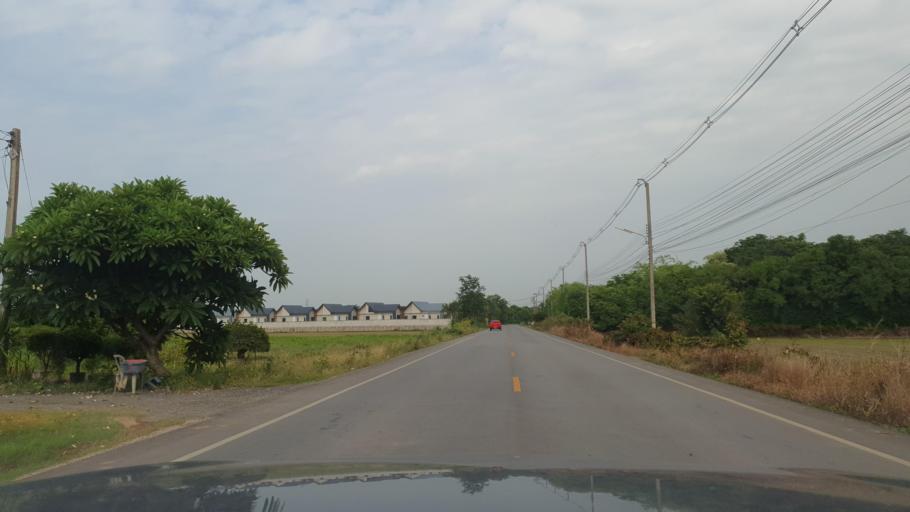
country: TH
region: Phitsanulok
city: Phitsanulok
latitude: 16.8143
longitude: 100.1901
